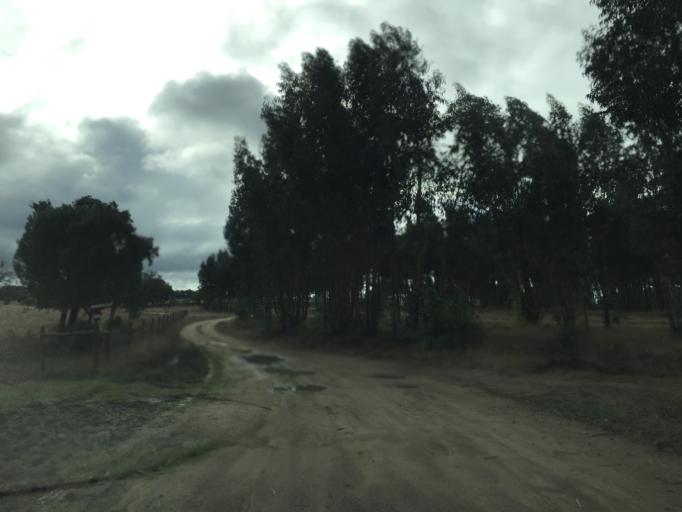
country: PT
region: Portalegre
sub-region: Alter do Chao
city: Alter do Chao
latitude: 39.2410
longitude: -7.7009
